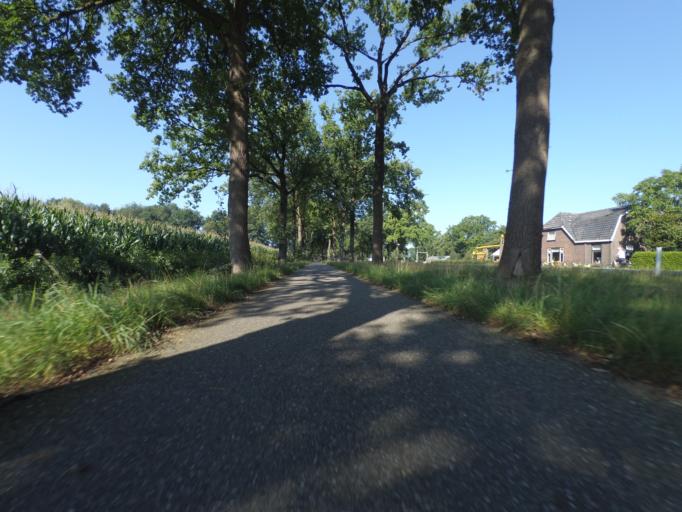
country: NL
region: Gelderland
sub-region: Gemeente Ede
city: Ederveen
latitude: 52.0469
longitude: 5.5880
